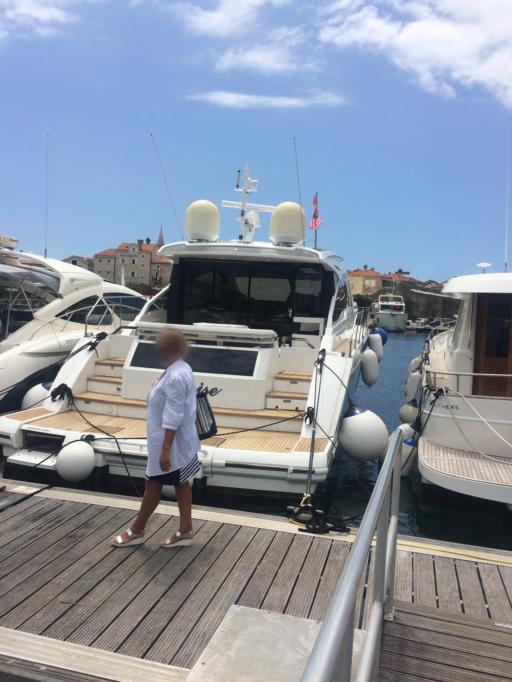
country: ME
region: Budva
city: Budva
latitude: 42.2801
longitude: 18.8382
